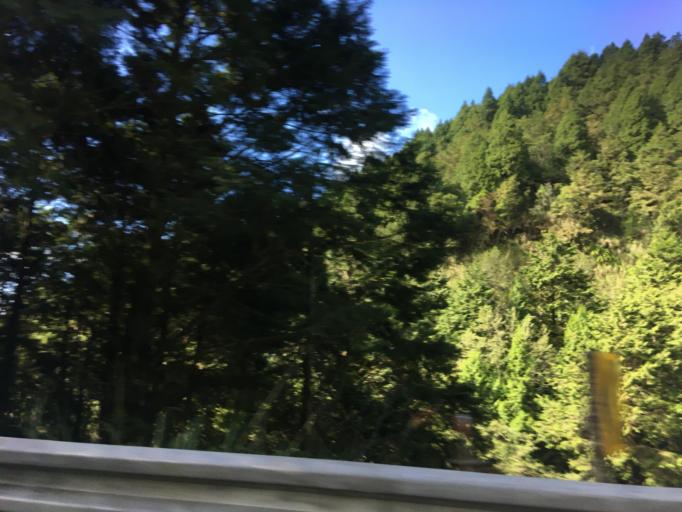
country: TW
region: Taiwan
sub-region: Yilan
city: Yilan
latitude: 24.5141
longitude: 121.5875
